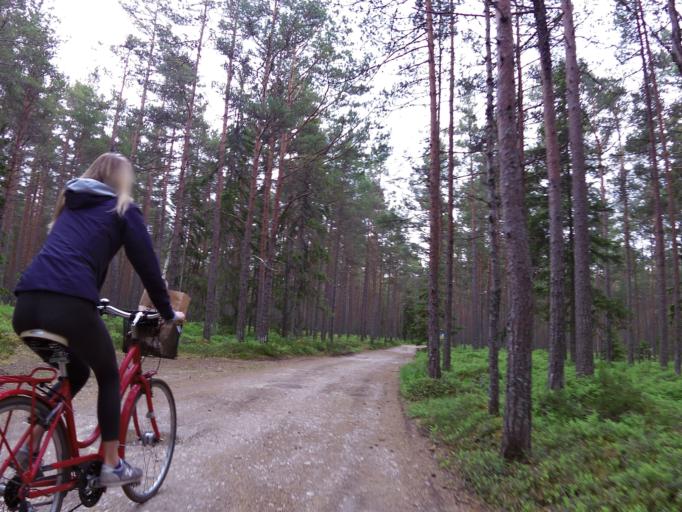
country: EE
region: Harju
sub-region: Paldiski linn
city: Paldiski
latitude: 59.2496
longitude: 23.7496
